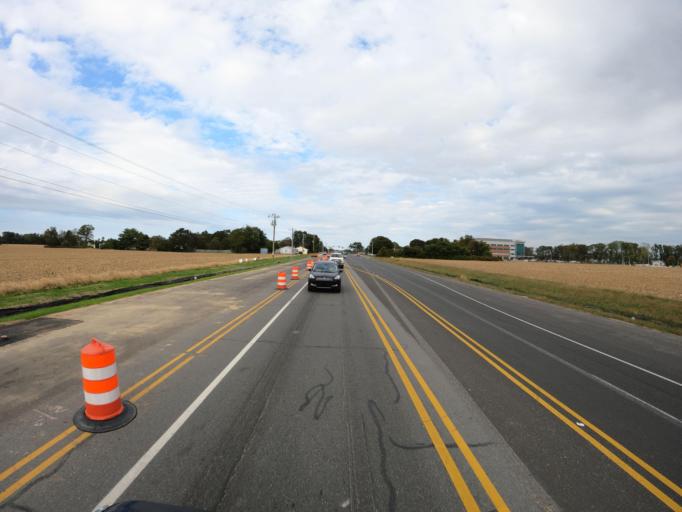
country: US
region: Delaware
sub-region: Sussex County
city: Lewes
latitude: 38.7217
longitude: -75.1448
